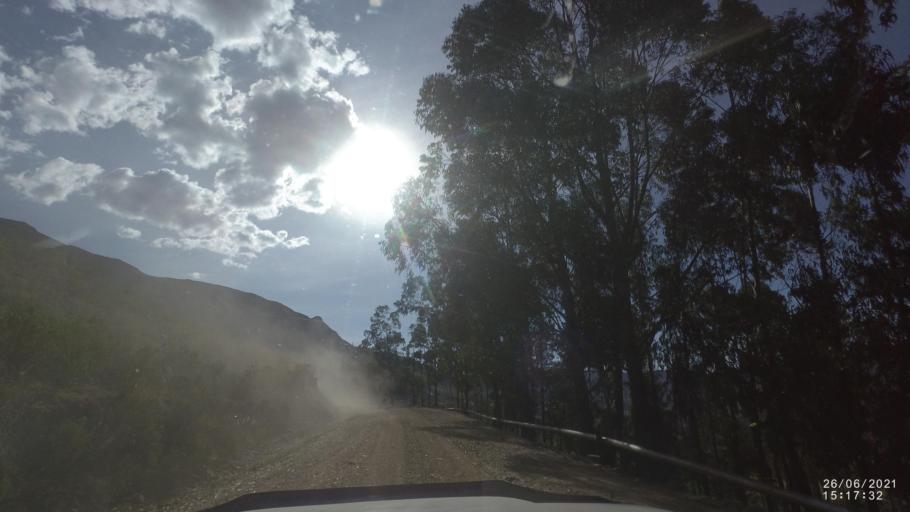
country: BO
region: Cochabamba
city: Mizque
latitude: -17.9518
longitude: -65.6513
